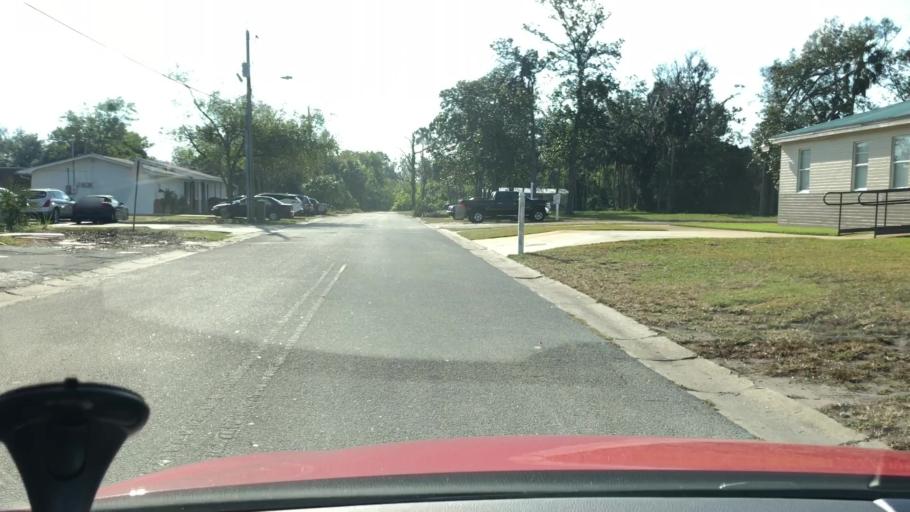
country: US
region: Florida
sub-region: Volusia County
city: Holly Hill
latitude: 29.2175
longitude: -81.0523
